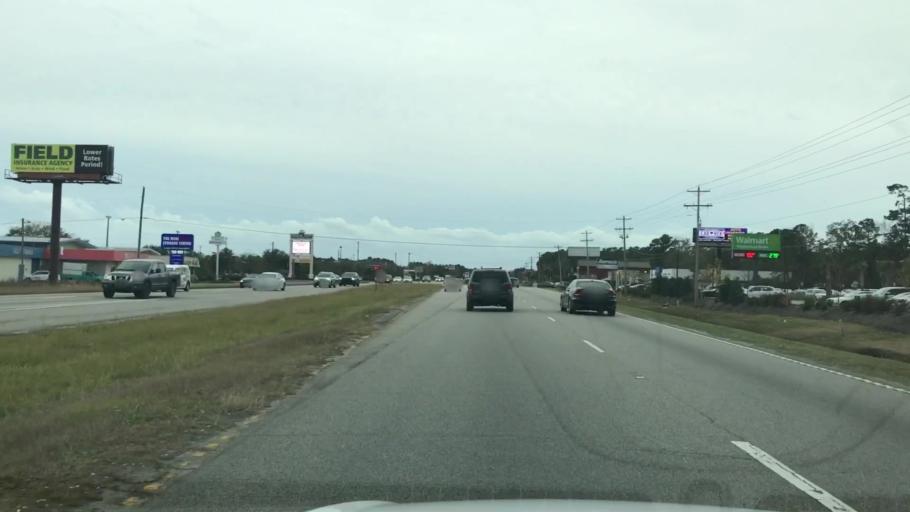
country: US
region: South Carolina
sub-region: Horry County
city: Garden City
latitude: 33.5843
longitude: -79.0276
